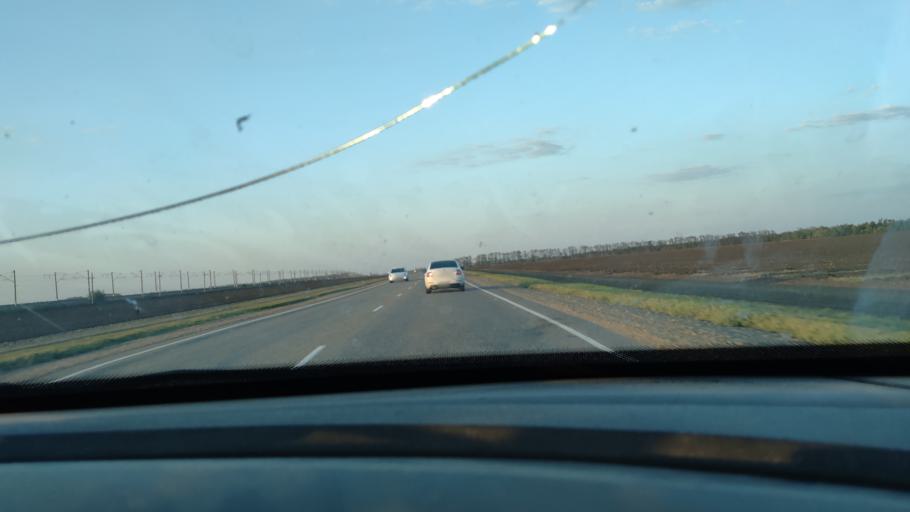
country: RU
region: Krasnodarskiy
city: Novominskaya
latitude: 46.3405
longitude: 38.9526
